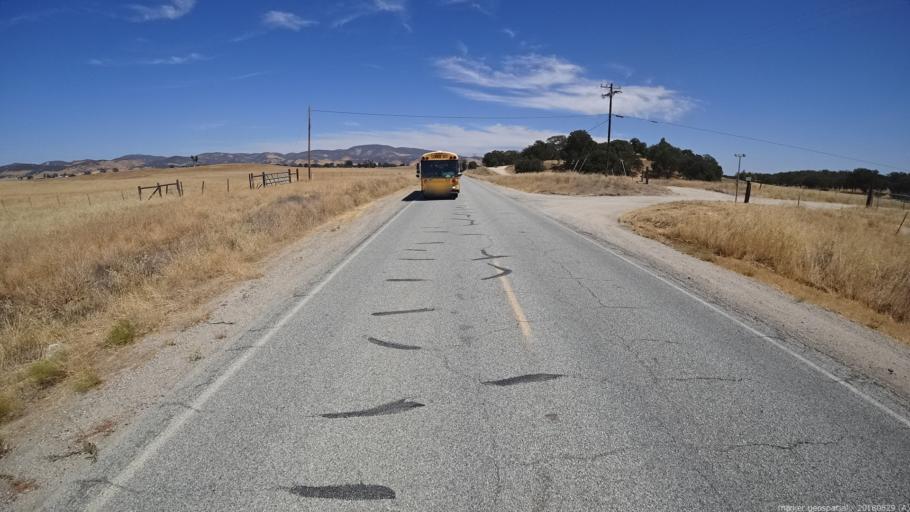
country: US
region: California
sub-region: Monterey County
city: King City
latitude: 35.9371
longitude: -121.1002
